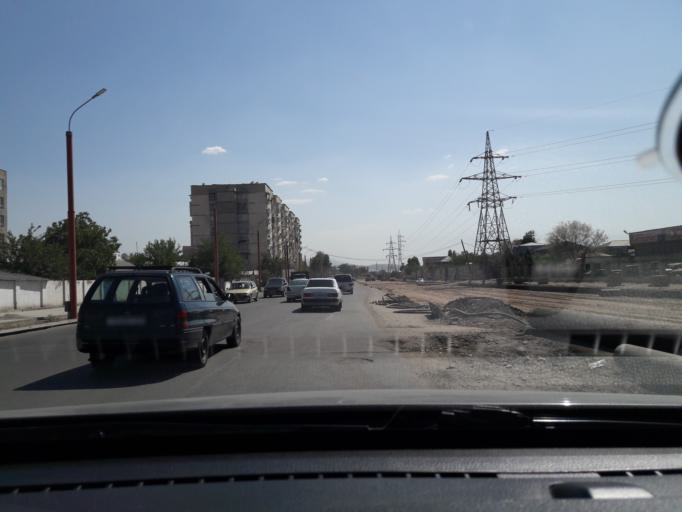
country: TJ
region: Dushanbe
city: Dushanbe
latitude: 38.5357
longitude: 68.7403
